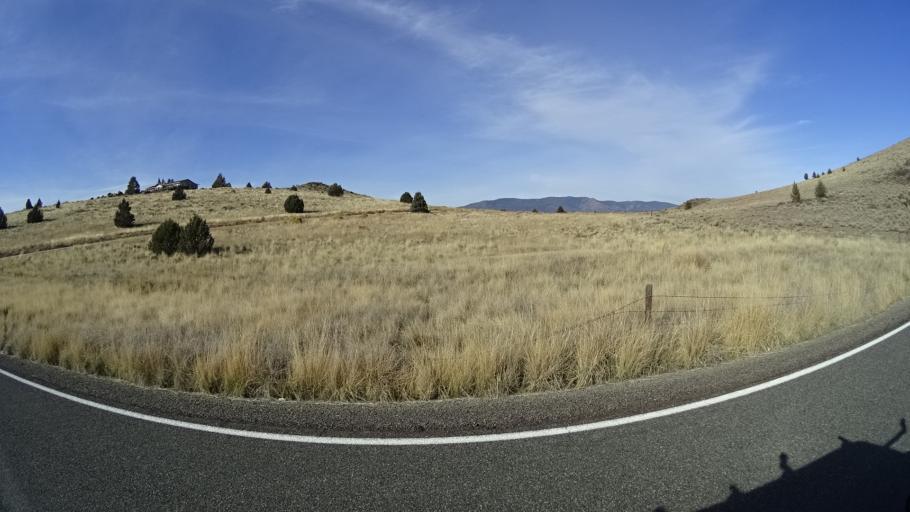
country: US
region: California
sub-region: Siskiyou County
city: Weed
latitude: 41.5391
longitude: -122.5037
